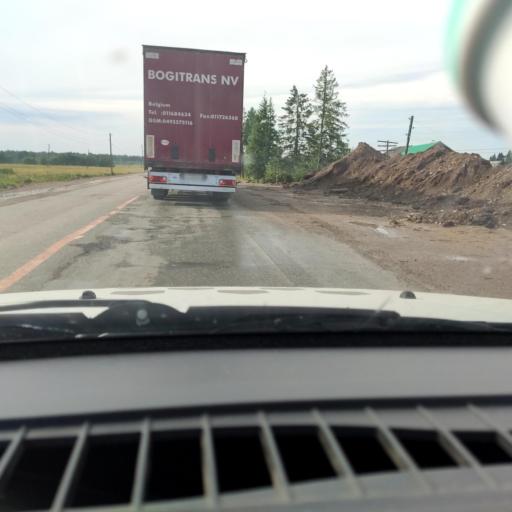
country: RU
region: Kirov
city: Kostino
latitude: 58.8307
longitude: 53.3081
